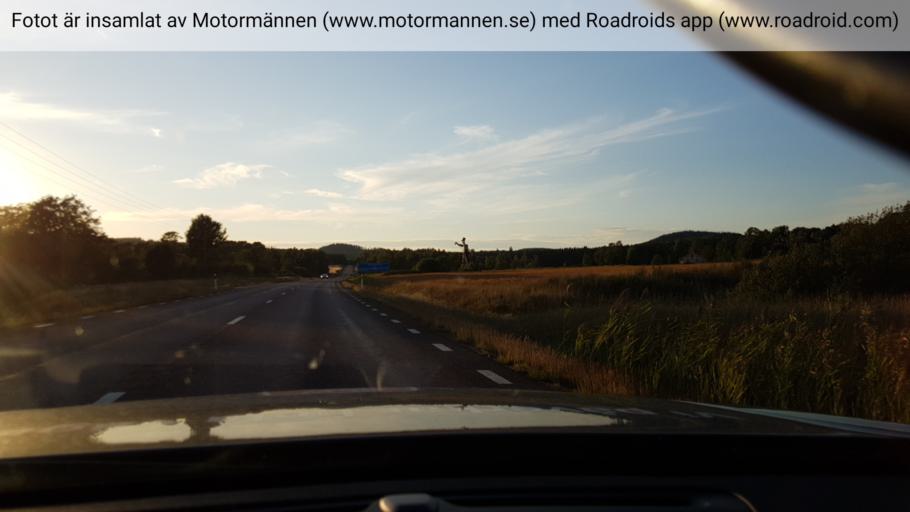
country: SE
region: OErebro
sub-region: Karlskoga Kommun
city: Karlskoga
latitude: 59.4353
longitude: 14.4112
